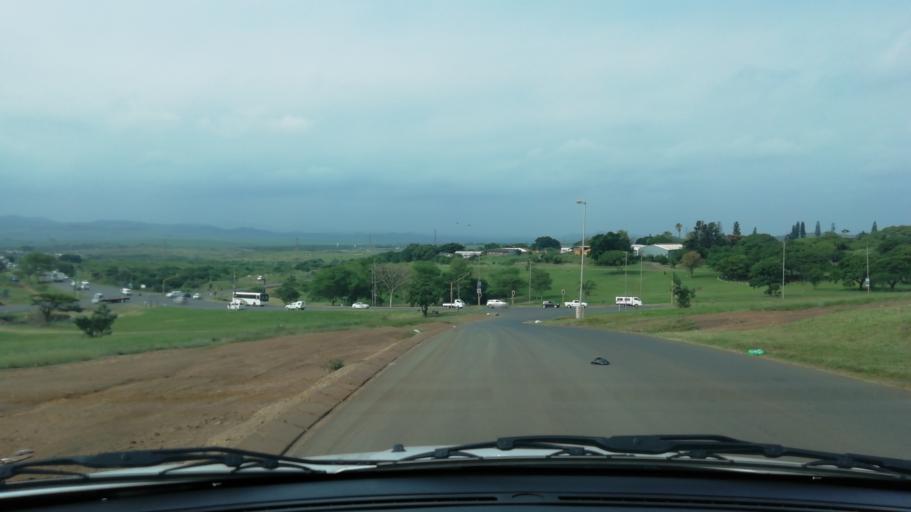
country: ZA
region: KwaZulu-Natal
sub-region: uThungulu District Municipality
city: Empangeni
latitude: -28.7439
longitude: 31.8821
